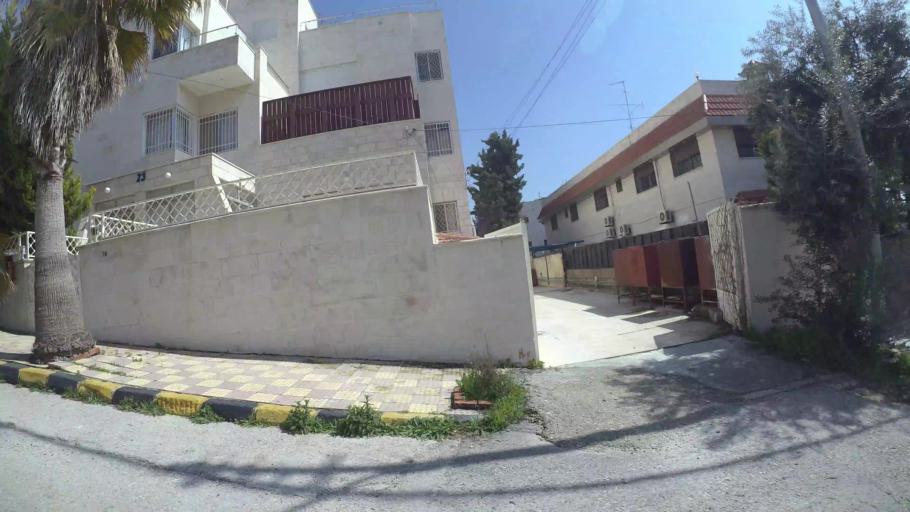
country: JO
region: Amman
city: Al Bunayyat ash Shamaliyah
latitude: 31.8851
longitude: 35.8959
